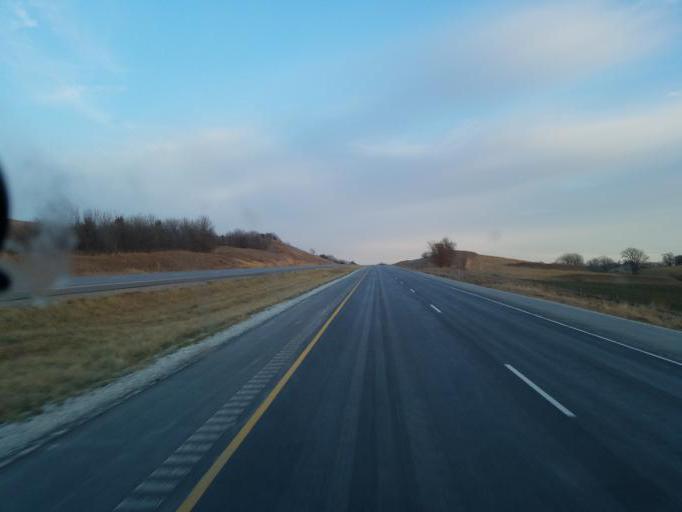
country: US
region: Iowa
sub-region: Harrison County
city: Logan
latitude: 41.4981
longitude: -95.6665
